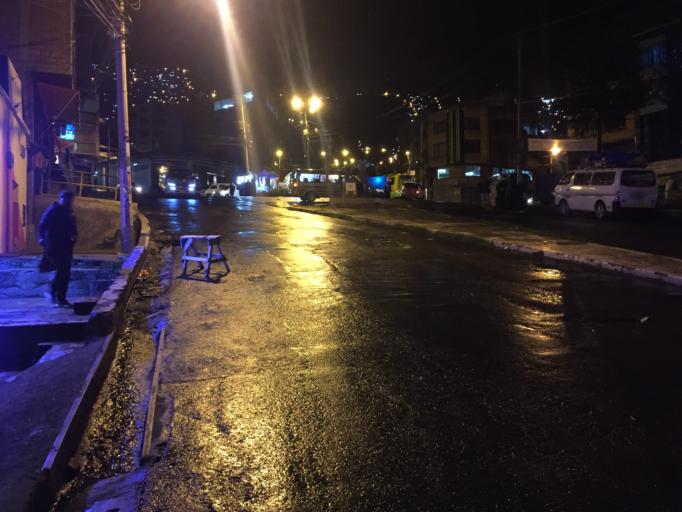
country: BO
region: La Paz
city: La Paz
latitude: -16.5002
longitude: -68.1525
